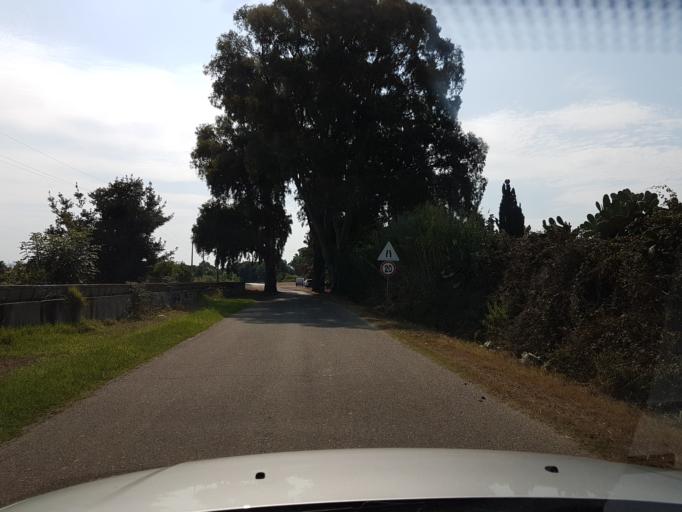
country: IT
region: Sardinia
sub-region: Provincia di Oristano
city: Donigala Fenugheddu
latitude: 39.9370
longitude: 8.5767
